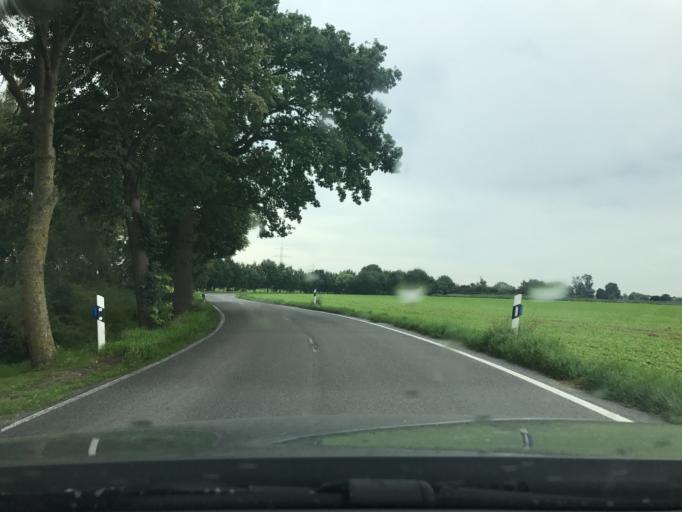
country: DE
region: North Rhine-Westphalia
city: Tonisvorst
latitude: 51.3539
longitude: 6.5003
